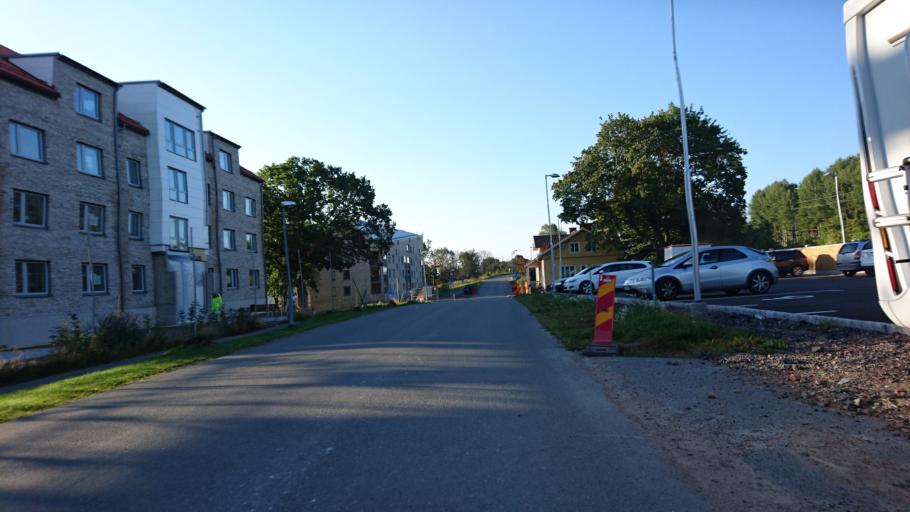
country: SE
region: Joenkoeping
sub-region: Jonkopings Kommun
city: Jonkoping
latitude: 57.8118
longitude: 14.1525
